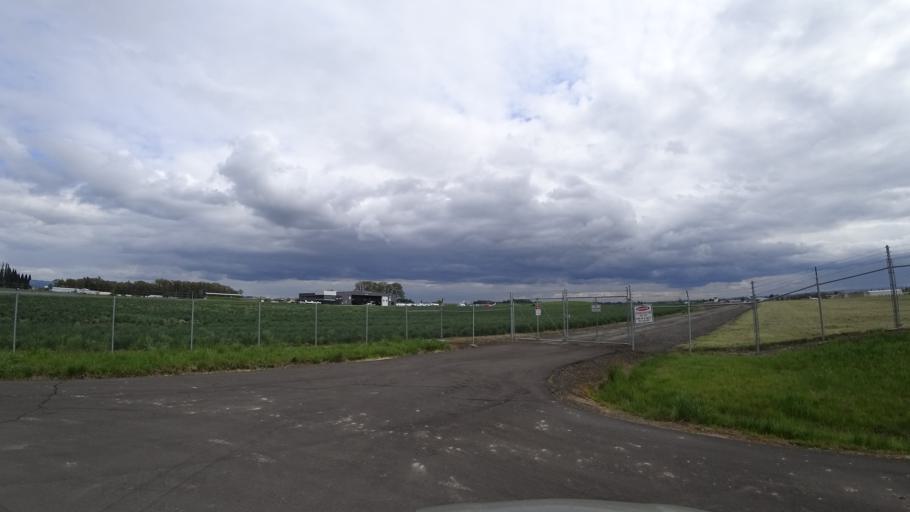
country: US
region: Oregon
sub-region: Washington County
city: Hillsboro
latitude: 45.5498
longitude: -122.9529
